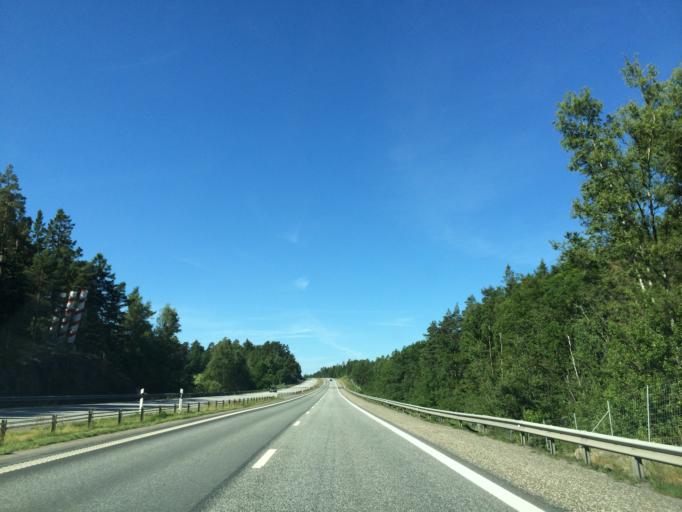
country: SE
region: Joenkoeping
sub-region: Jonkopings Kommun
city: Graenna
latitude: 57.9731
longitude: 14.3811
